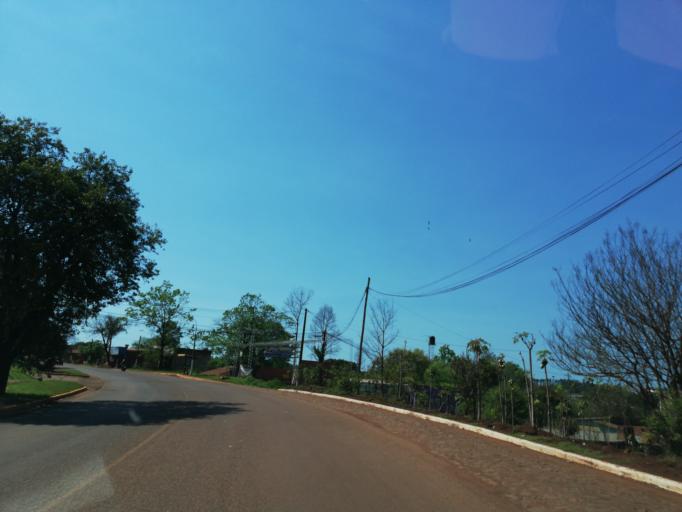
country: AR
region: Misiones
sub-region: Departamento de Eldorado
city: Eldorado
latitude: -26.4092
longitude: -54.6460
